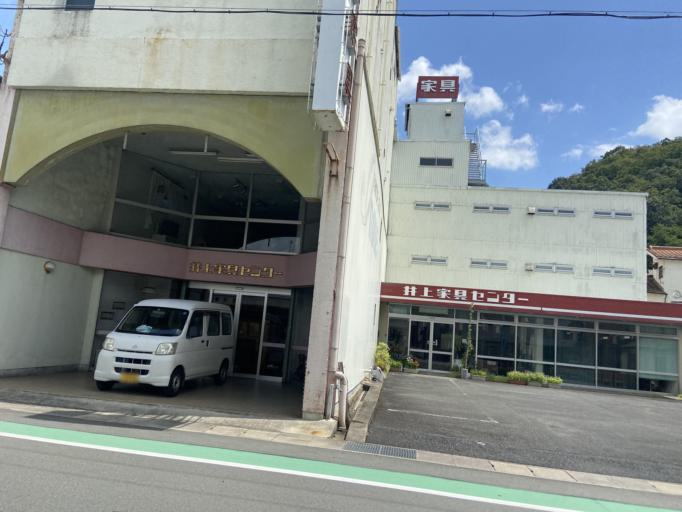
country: JP
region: Hyogo
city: Yamazakicho-nakabirose
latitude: 35.0051
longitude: 134.3579
